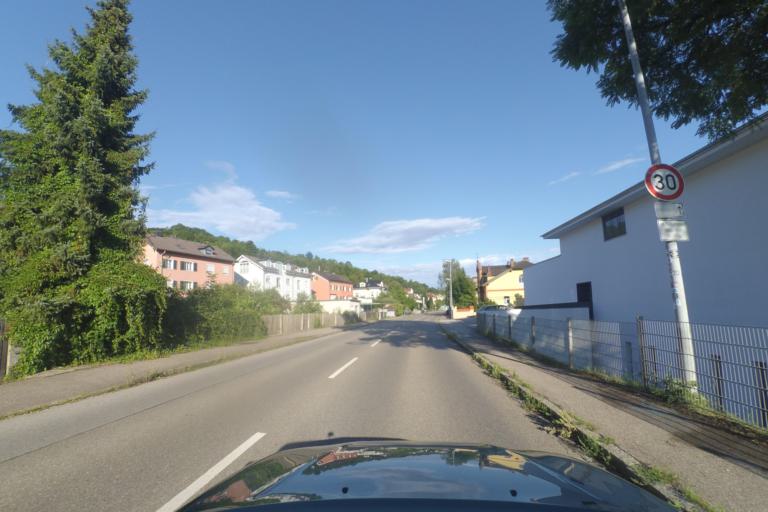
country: DE
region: Bavaria
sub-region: Upper Bavaria
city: Eichstaett
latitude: 48.8881
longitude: 11.1954
